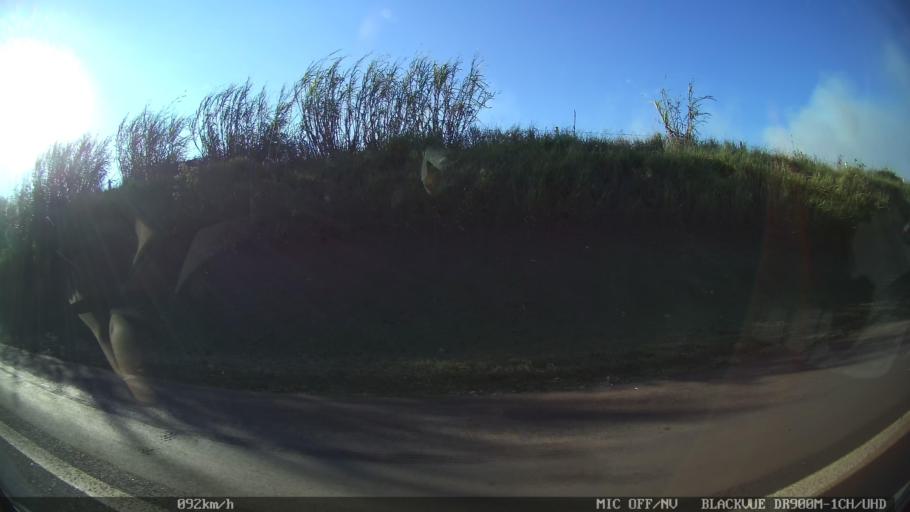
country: BR
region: Sao Paulo
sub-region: Piracicaba
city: Piracicaba
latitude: -22.6986
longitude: -47.6083
